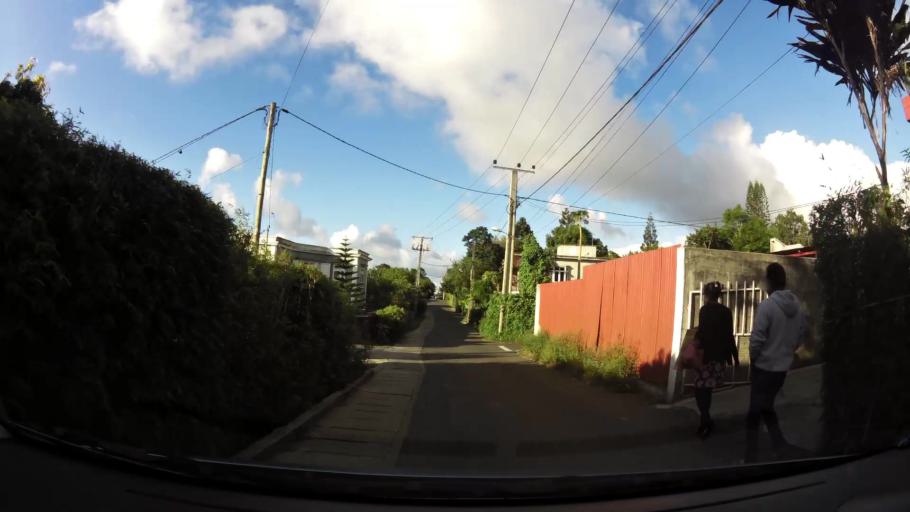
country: MU
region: Plaines Wilhems
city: Curepipe
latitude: -20.3144
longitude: 57.5136
